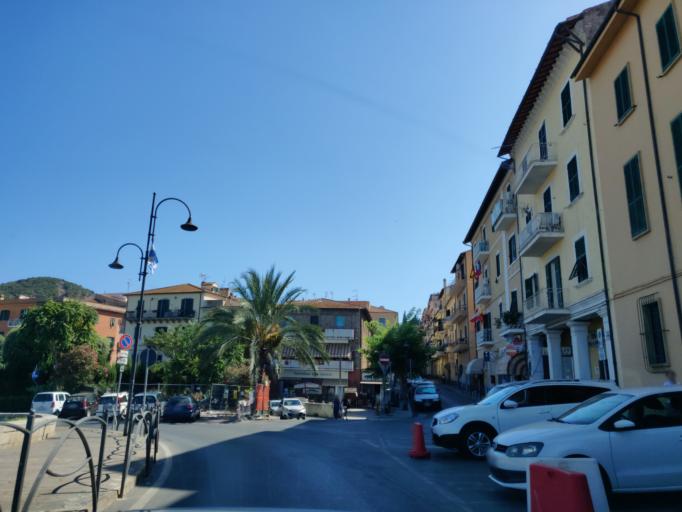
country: IT
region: Tuscany
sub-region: Provincia di Grosseto
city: Monte Argentario
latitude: 42.4356
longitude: 11.1206
